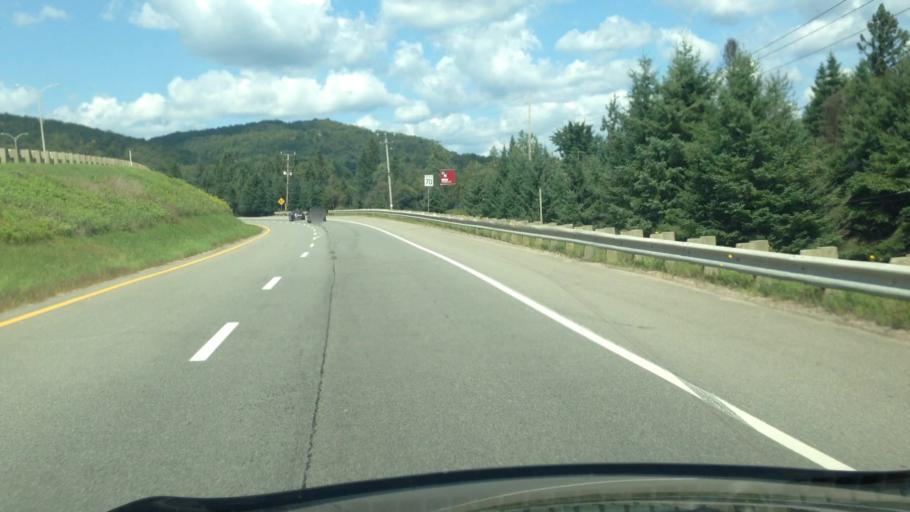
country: CA
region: Quebec
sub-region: Laurentides
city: Mont-Tremblant
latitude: 46.1298
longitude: -74.6102
